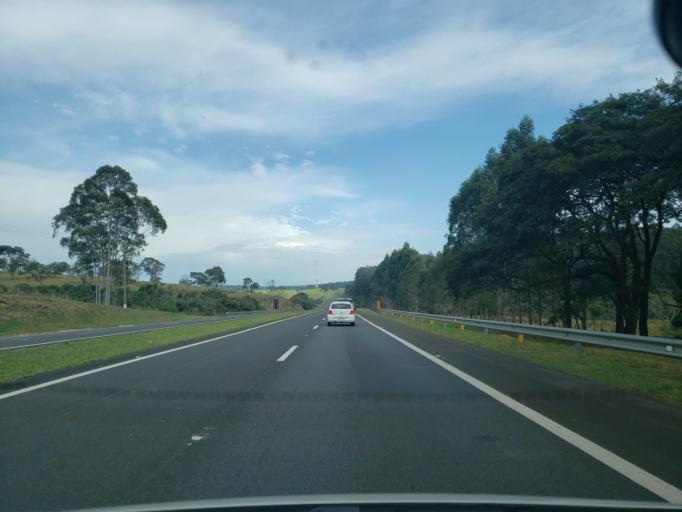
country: BR
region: Sao Paulo
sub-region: Itirapina
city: Itirapina
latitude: -22.2742
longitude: -47.9610
